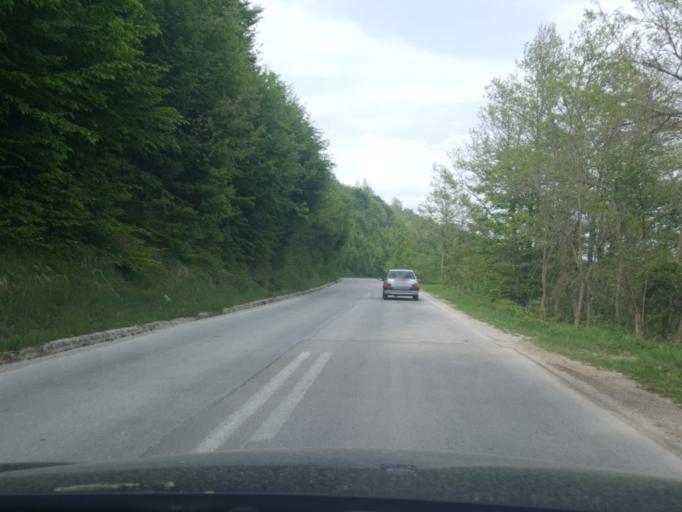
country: RS
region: Central Serbia
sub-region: Zlatiborski Okrug
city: Bajina Basta
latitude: 44.0948
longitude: 19.6638
